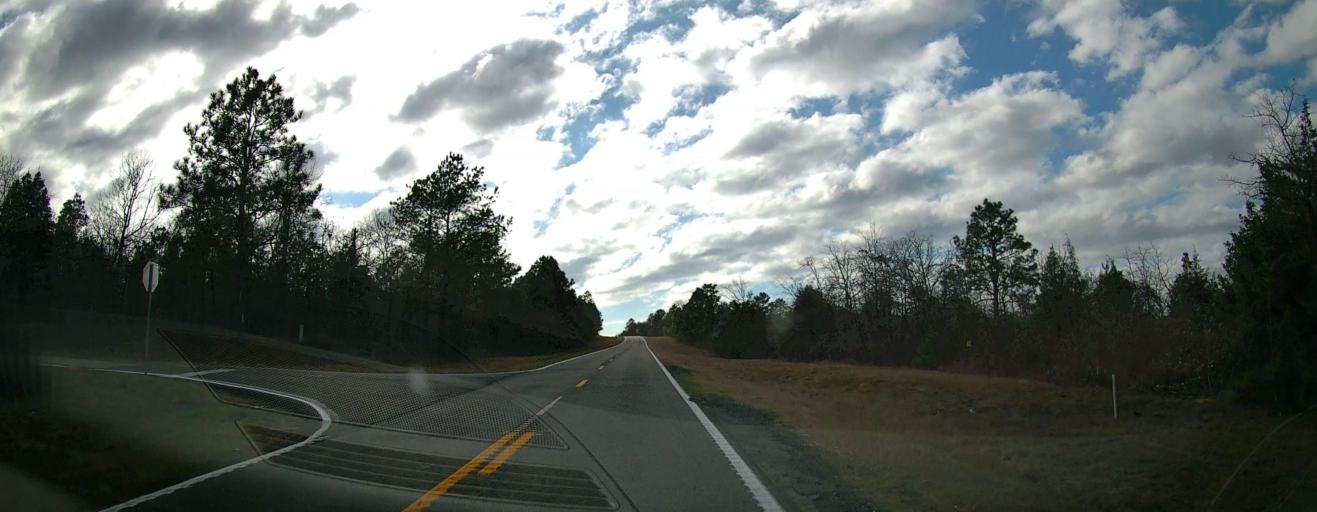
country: US
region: Georgia
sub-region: Marion County
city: Buena Vista
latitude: 32.4405
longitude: -84.4902
